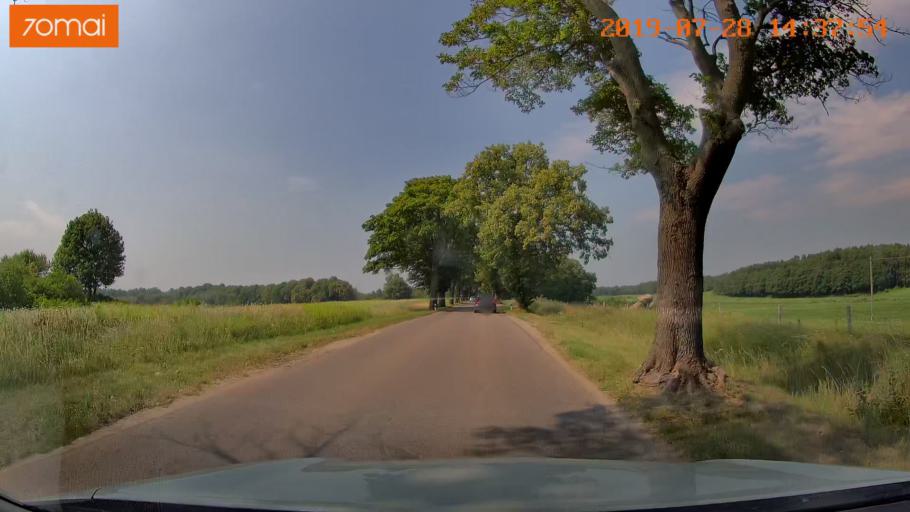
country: RU
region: Kaliningrad
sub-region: Gorod Kaliningrad
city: Yantarnyy
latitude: 54.8422
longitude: 19.9911
